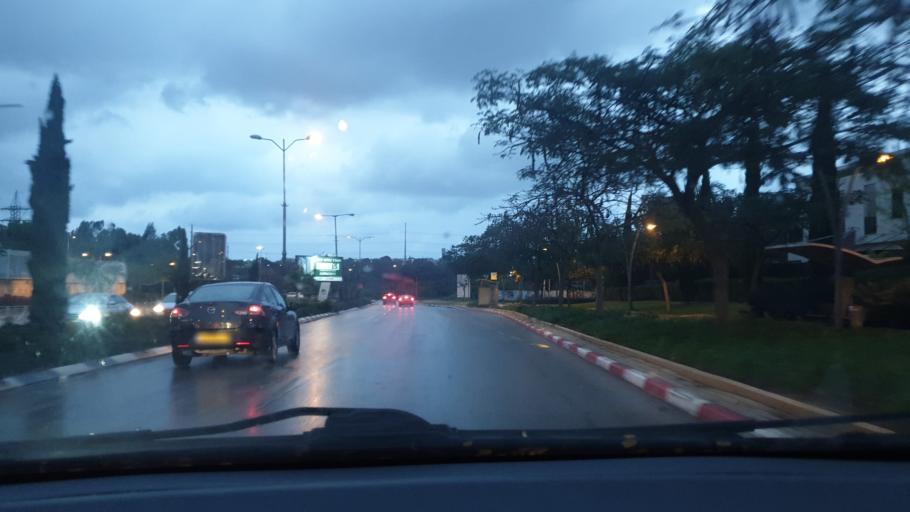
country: IL
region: Central District
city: Rishon LeZiyyon
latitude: 31.9826
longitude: 34.8018
